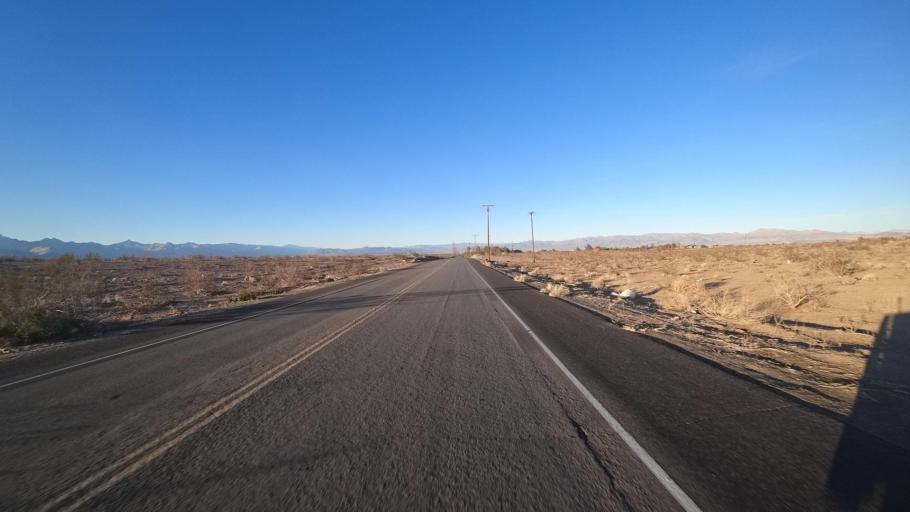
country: US
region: California
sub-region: Kern County
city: China Lake Acres
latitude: 35.6180
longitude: -117.7230
